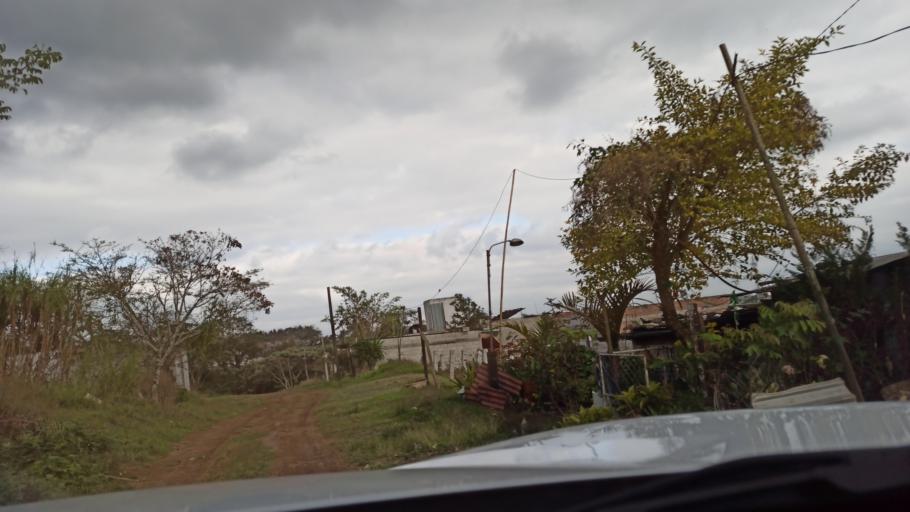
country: MX
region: Veracruz
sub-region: Fortin
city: Fortin de las Flores
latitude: 18.9176
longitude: -97.0031
